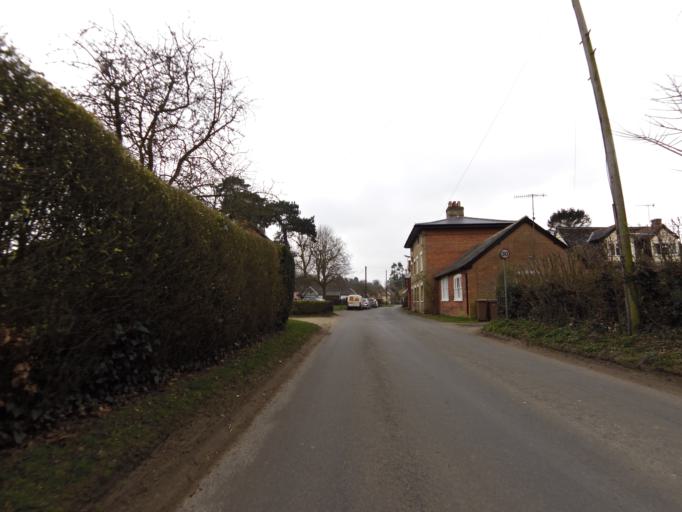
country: GB
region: England
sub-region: Suffolk
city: Cookley
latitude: 52.2735
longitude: 1.4552
